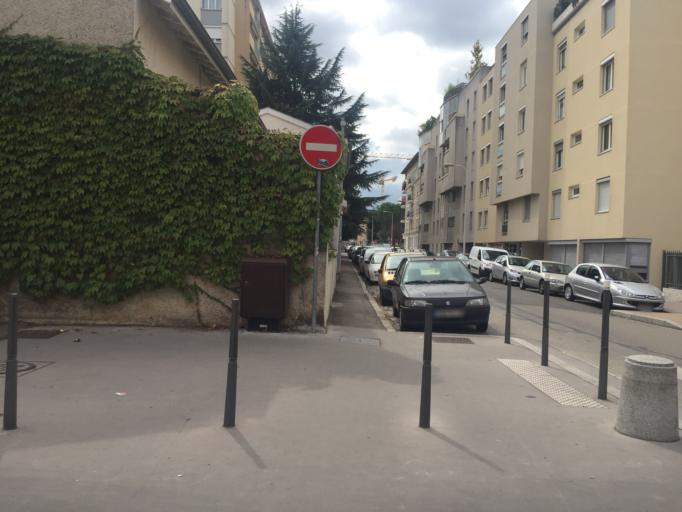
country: FR
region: Rhone-Alpes
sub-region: Departement du Rhone
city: Lyon
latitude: 45.7440
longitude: 4.8632
